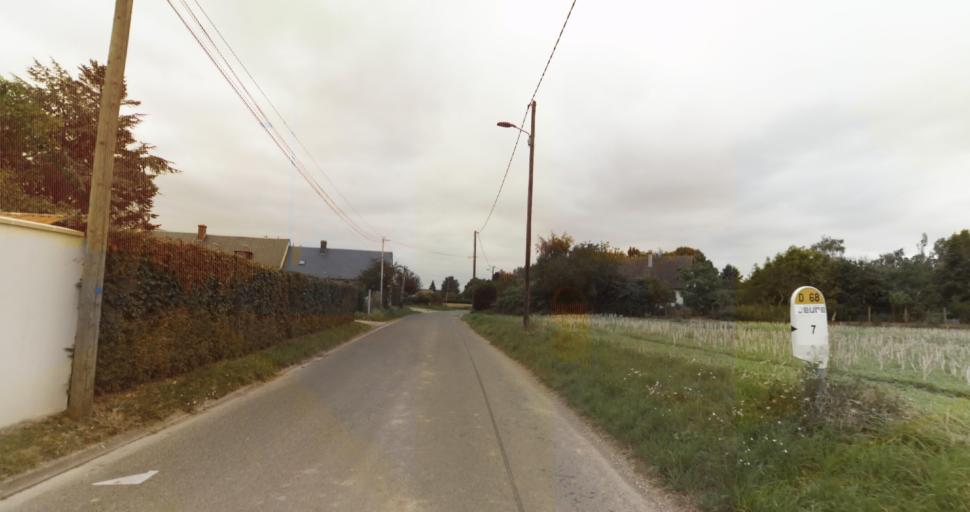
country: FR
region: Haute-Normandie
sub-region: Departement de l'Eure
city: La Couture-Boussey
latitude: 48.9280
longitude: 1.3246
